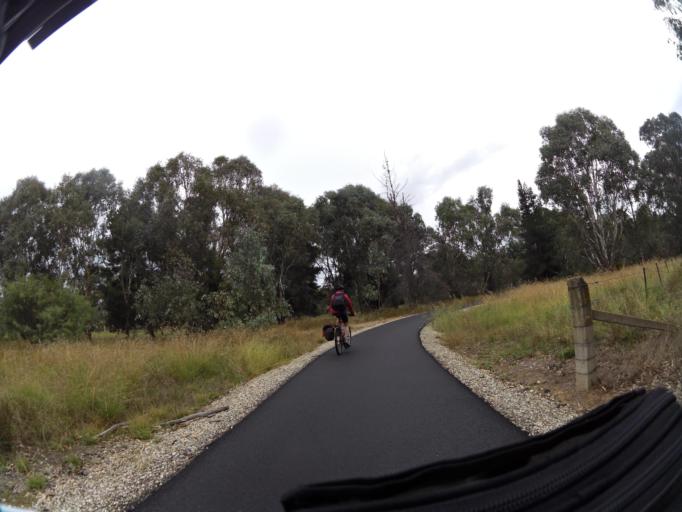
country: AU
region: Victoria
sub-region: Wodonga
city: Wodonga
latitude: -36.1485
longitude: 146.9280
